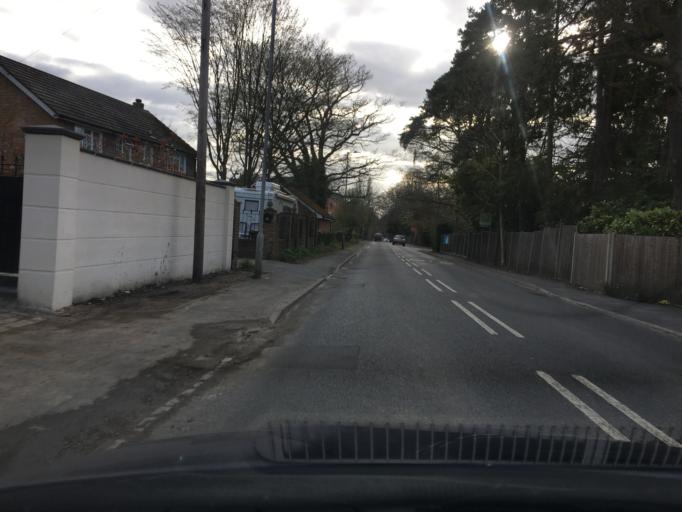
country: GB
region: England
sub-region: Bracknell Forest
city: Crowthorne
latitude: 51.3695
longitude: -0.8046
